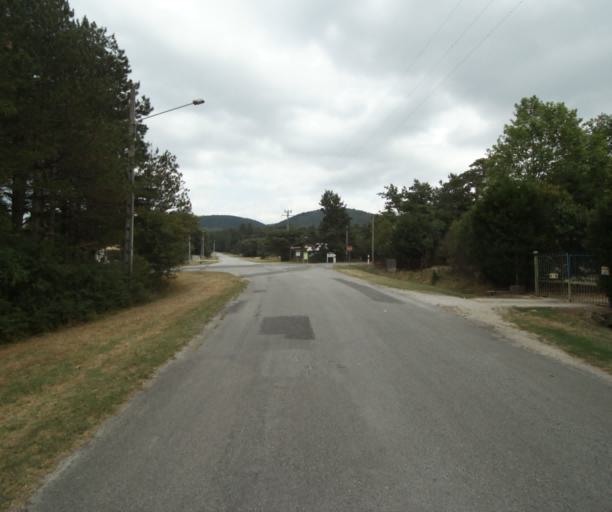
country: FR
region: Midi-Pyrenees
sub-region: Departement de la Haute-Garonne
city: Revel
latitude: 43.4327
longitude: 2.0168
